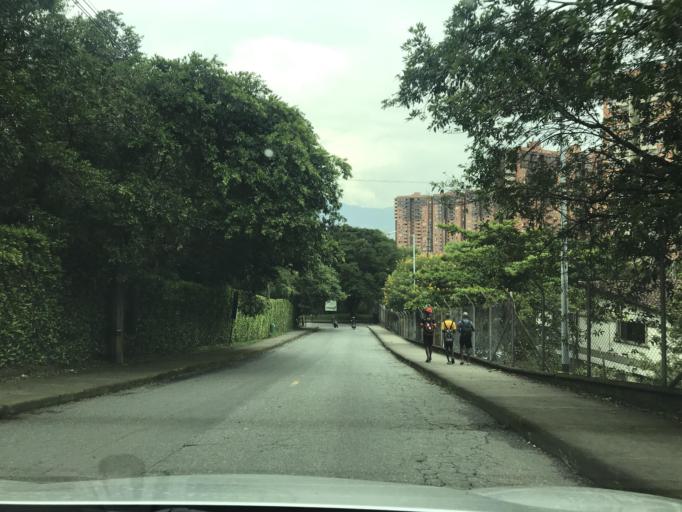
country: CO
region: Antioquia
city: Medellin
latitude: 6.2675
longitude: -75.6036
